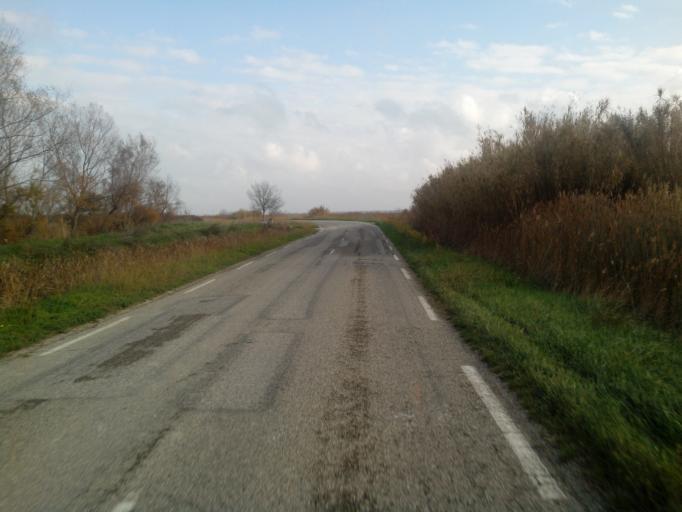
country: FR
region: Provence-Alpes-Cote d'Azur
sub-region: Departement des Bouches-du-Rhone
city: Arles
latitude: 43.5659
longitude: 4.5762
